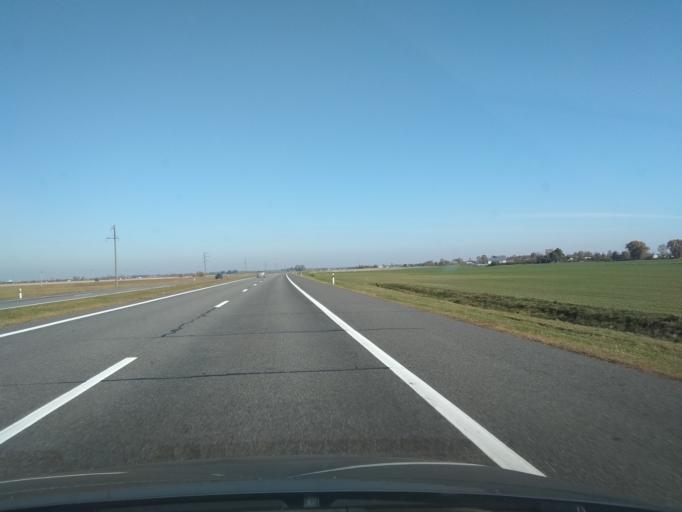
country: BY
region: Brest
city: Byaroza
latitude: 52.4765
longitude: 24.9427
